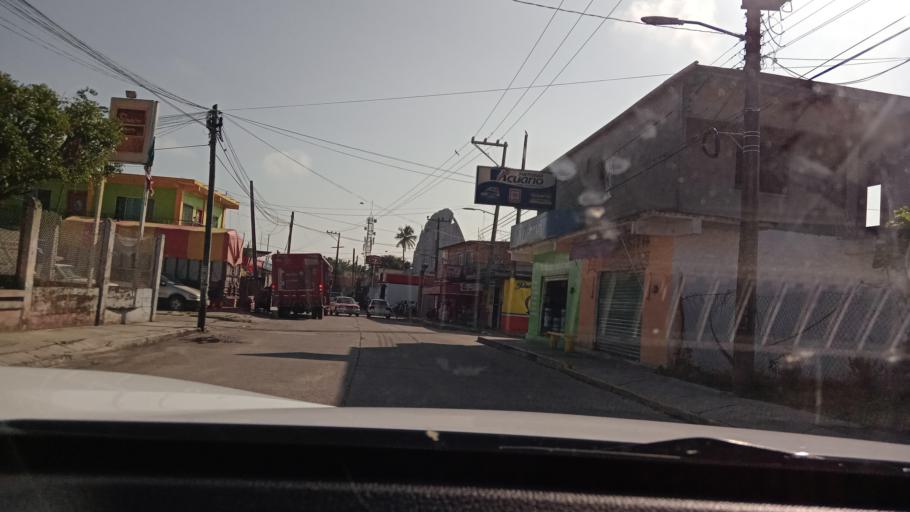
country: MX
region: Veracruz
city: Las Choapas
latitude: 17.8949
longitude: -94.1029
